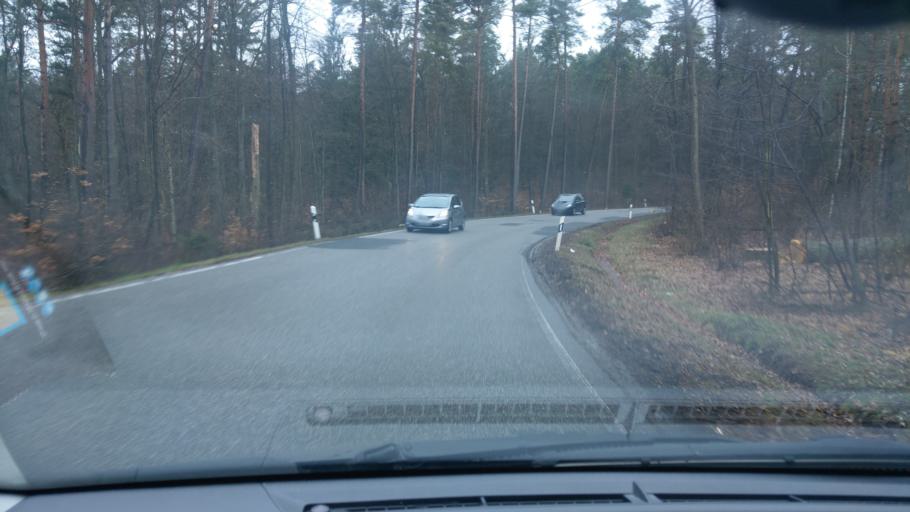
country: DE
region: Rheinland-Pfalz
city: Bechhofen
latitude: 49.3569
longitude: 7.3840
